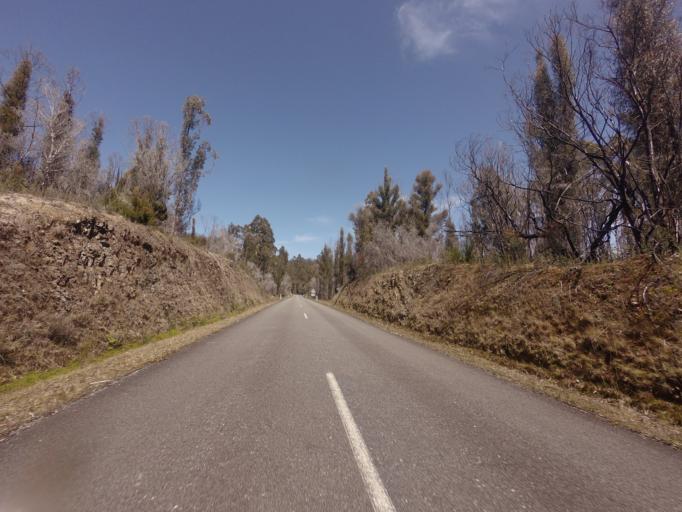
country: AU
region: Tasmania
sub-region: Huon Valley
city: Geeveston
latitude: -42.8337
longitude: 146.2677
